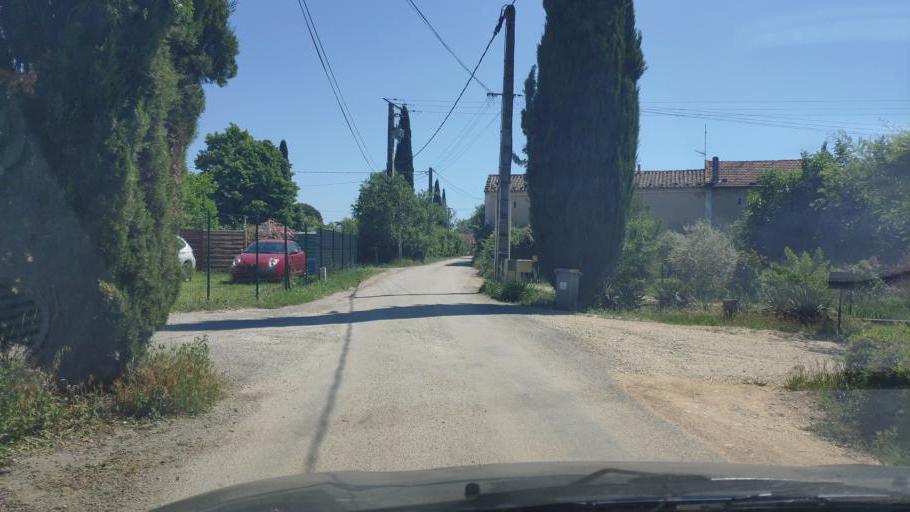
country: FR
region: Provence-Alpes-Cote d'Azur
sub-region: Departement du Vaucluse
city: Carpentras
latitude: 44.0745
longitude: 5.0552
